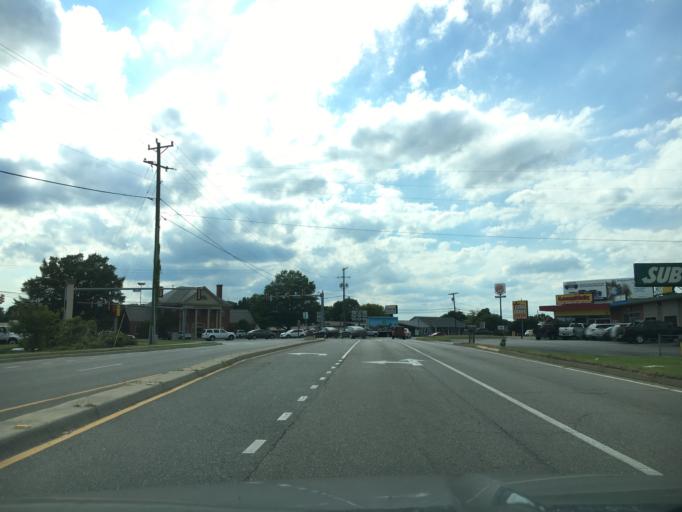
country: US
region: Virginia
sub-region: Halifax County
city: Halifax
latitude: 36.7355
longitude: -78.9173
